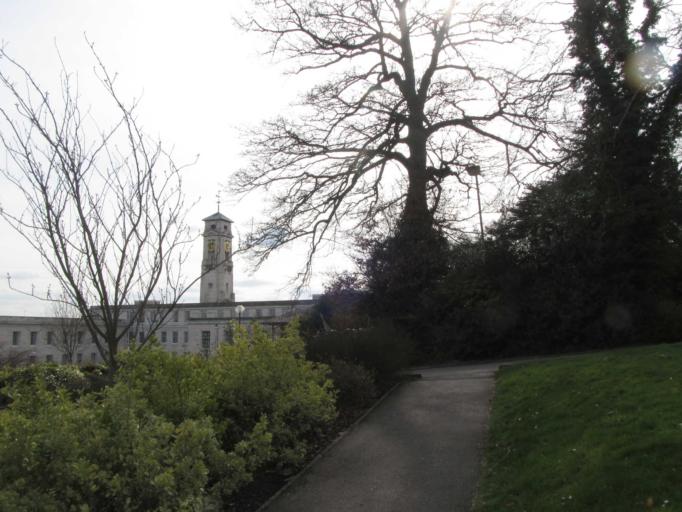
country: GB
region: England
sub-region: Nottingham
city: Nottingham
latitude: 52.9381
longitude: -1.1952
